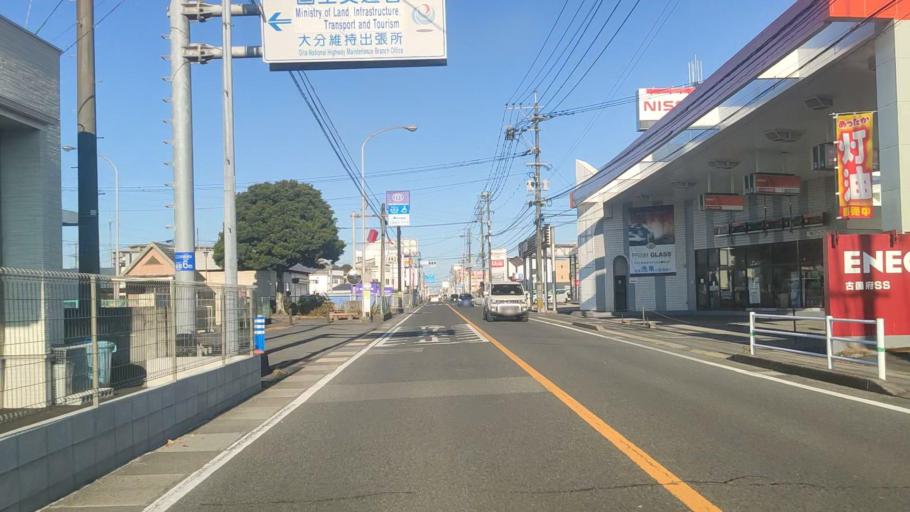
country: JP
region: Oita
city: Oita
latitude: 33.2144
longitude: 131.6107
